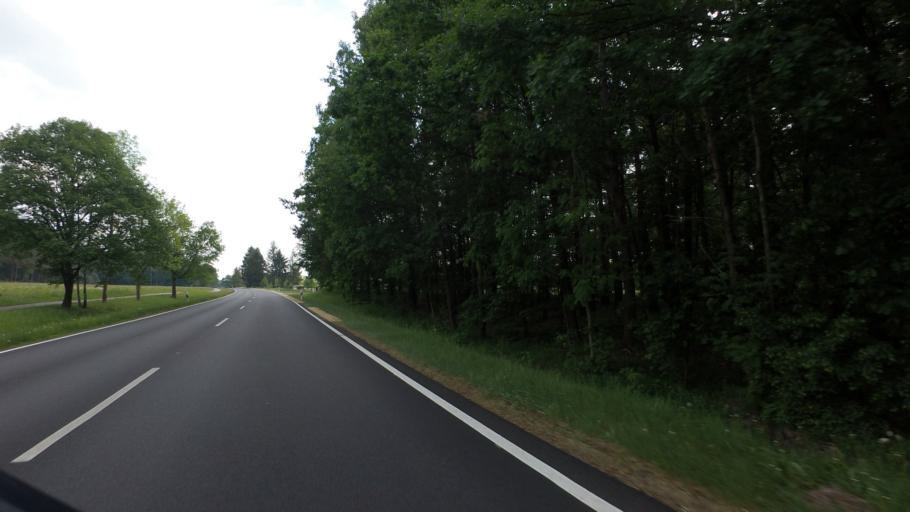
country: DE
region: Saxony
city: Rietschen
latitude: 51.3676
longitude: 14.7967
